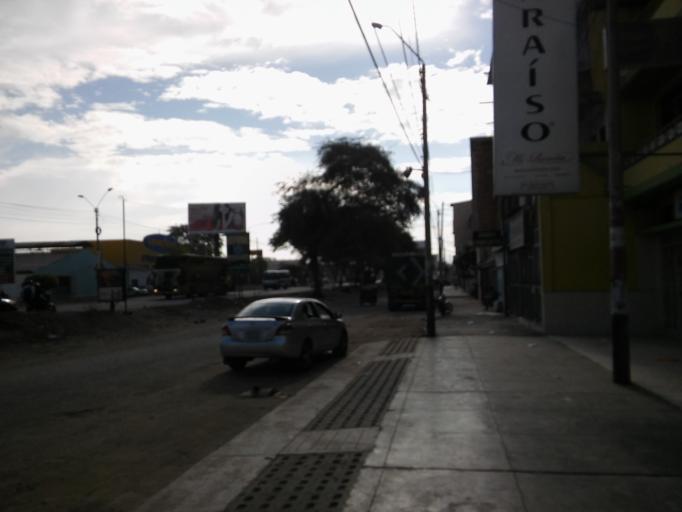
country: PE
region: Piura
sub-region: Provincia de Piura
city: Piura
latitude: -5.1880
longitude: -80.6406
